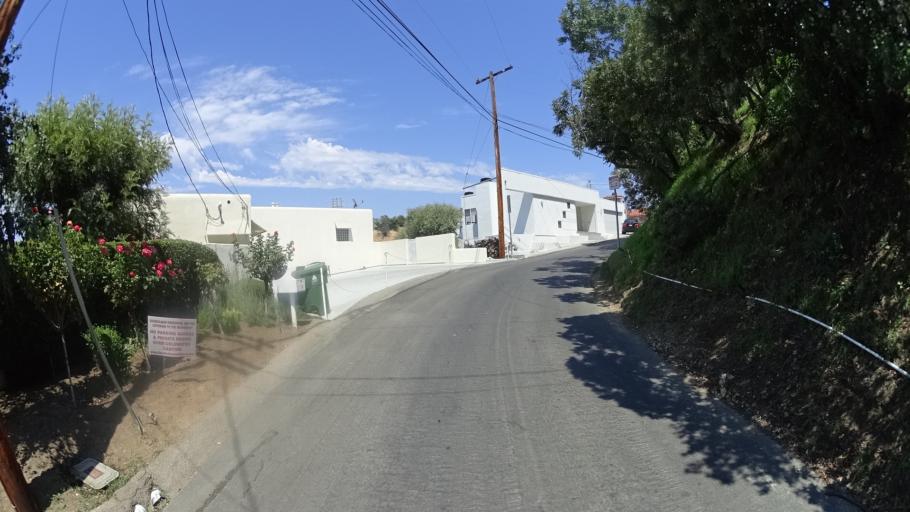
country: US
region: California
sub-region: Los Angeles County
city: Sherman Oaks
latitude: 34.1371
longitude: -118.4081
